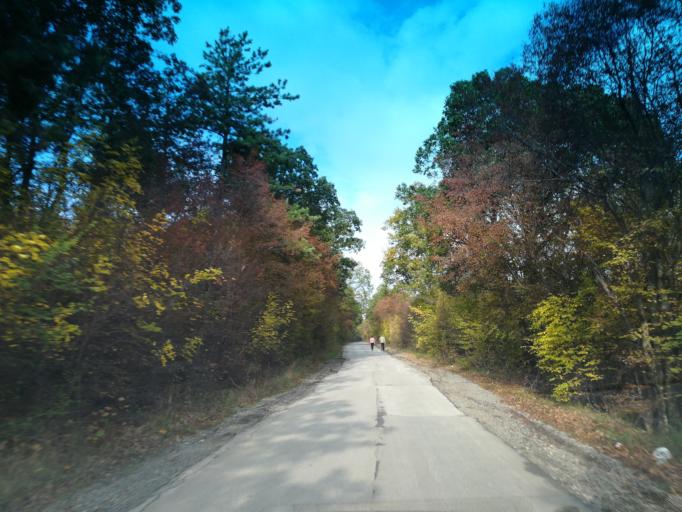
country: BG
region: Stara Zagora
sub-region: Obshtina Nikolaevo
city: Elkhovo
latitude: 42.3178
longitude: 25.4058
